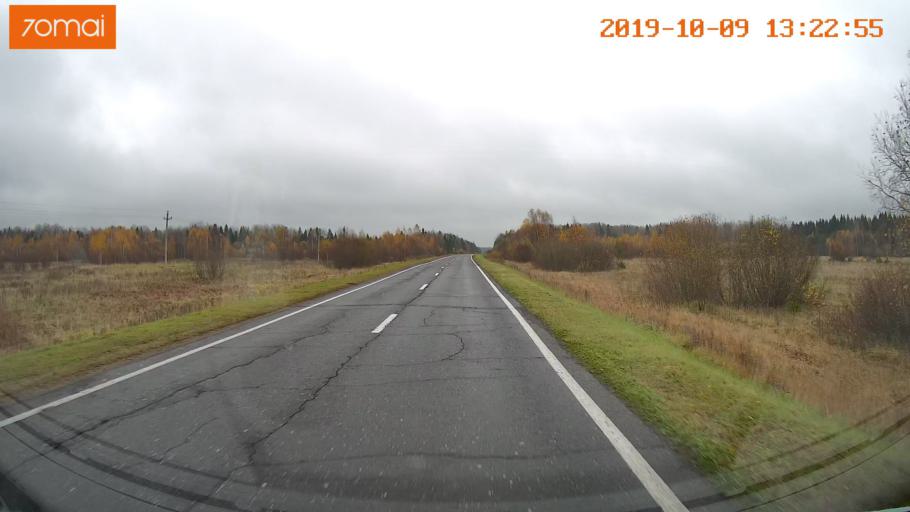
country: RU
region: Jaroslavl
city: Lyubim
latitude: 58.3379
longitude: 40.8761
